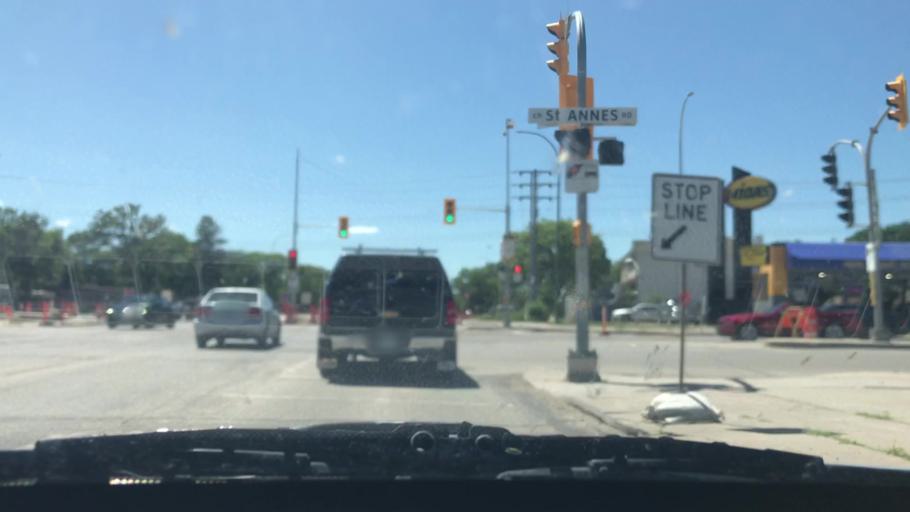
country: CA
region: Manitoba
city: Winnipeg
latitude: 49.8556
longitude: -97.1037
